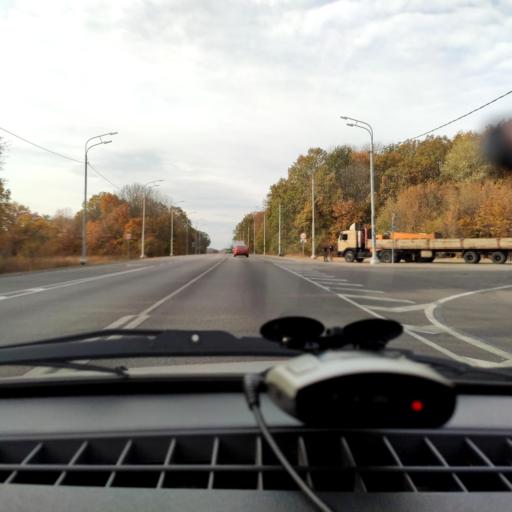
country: RU
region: Voronezj
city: Semiluki
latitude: 51.6493
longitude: 39.0301
